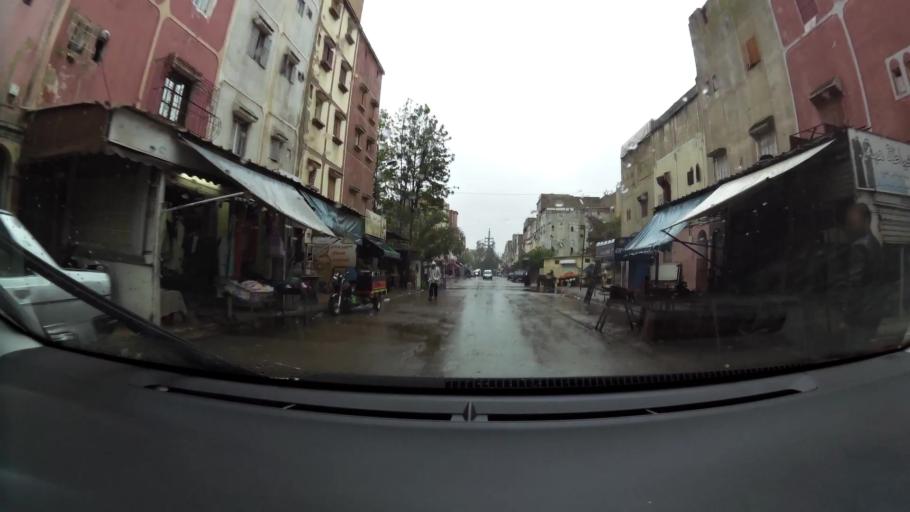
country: MA
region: Grand Casablanca
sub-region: Mediouna
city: Tit Mellil
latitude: 33.5687
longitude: -7.5273
